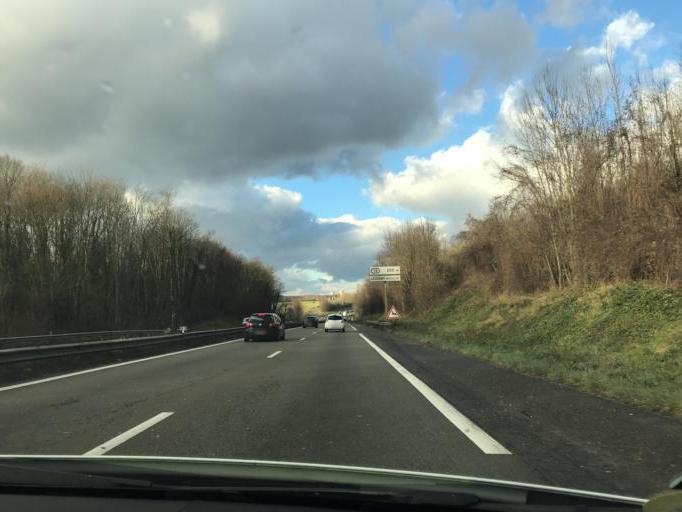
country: FR
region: Ile-de-France
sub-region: Departement de Seine-et-Marne
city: Servon
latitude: 48.7185
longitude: 2.5990
